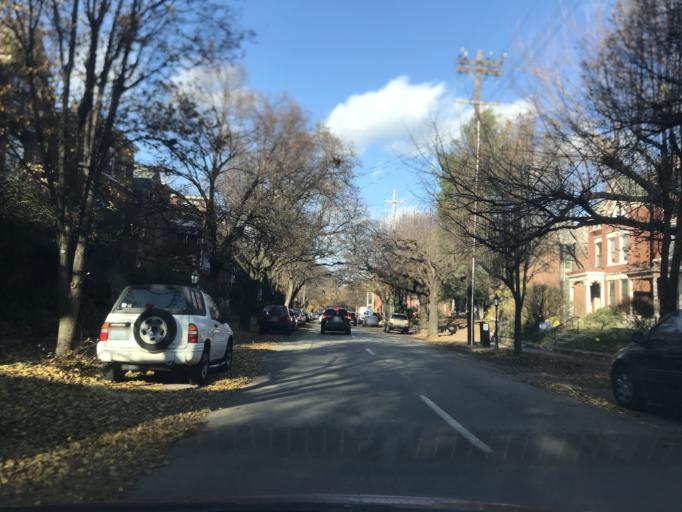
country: US
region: Kentucky
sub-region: Jefferson County
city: Louisville
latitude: 38.2260
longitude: -85.7586
